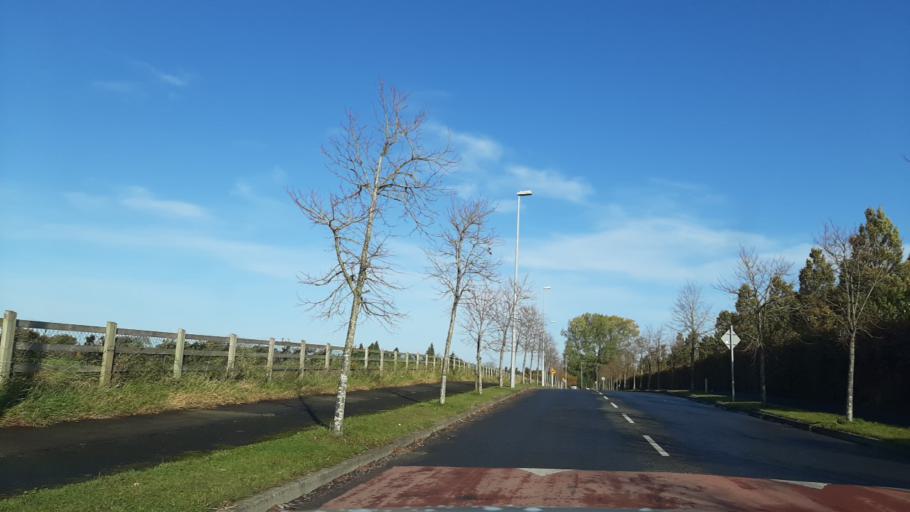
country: IE
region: Leinster
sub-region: Kildare
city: Rathangan
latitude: 53.2232
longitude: -7.0066
